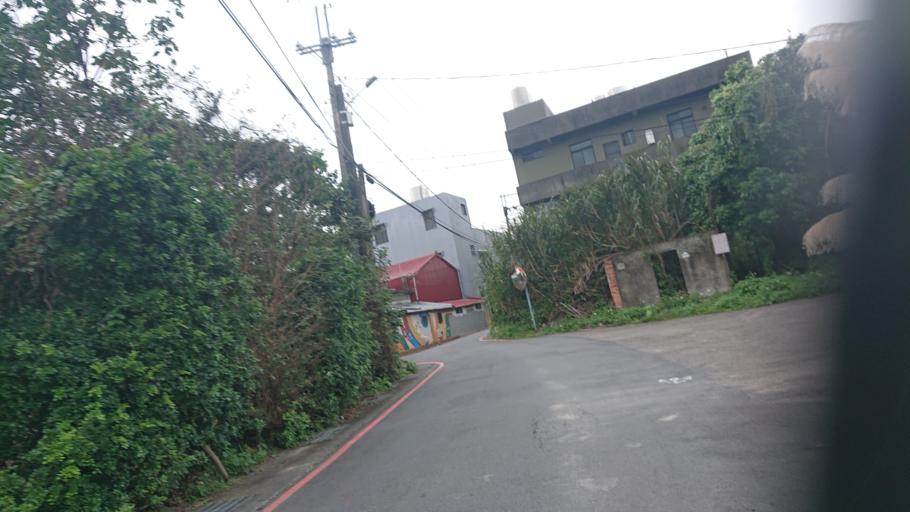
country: TW
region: Taiwan
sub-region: Taoyuan
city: Taoyuan
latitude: 24.9503
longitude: 121.3715
